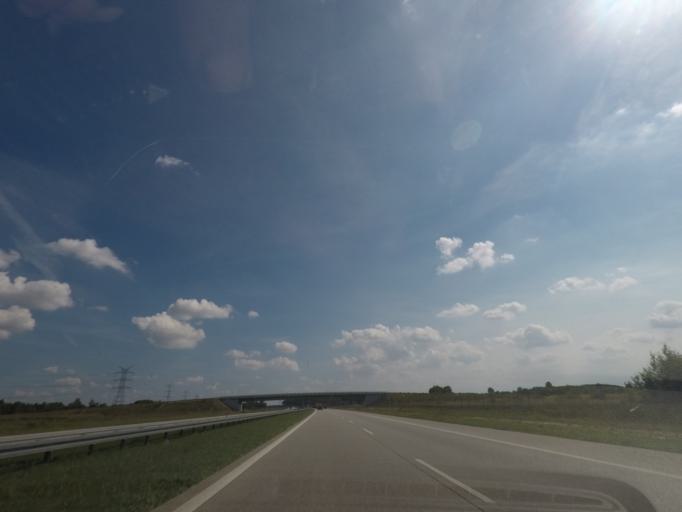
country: PL
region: Lodz Voivodeship
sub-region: Powiat lodzki wschodni
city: Tuszyn
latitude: 51.6156
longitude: 19.5701
